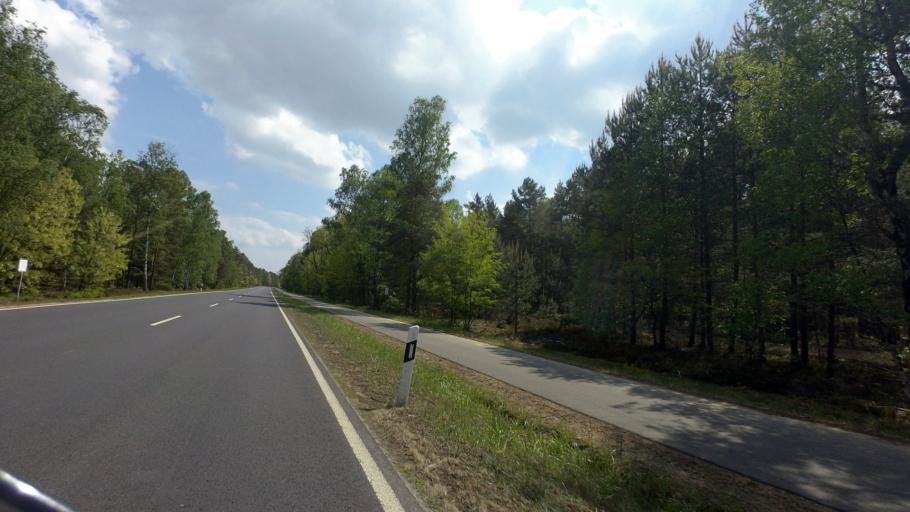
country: DE
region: Saxony
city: Rietschen
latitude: 51.4485
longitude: 14.7700
